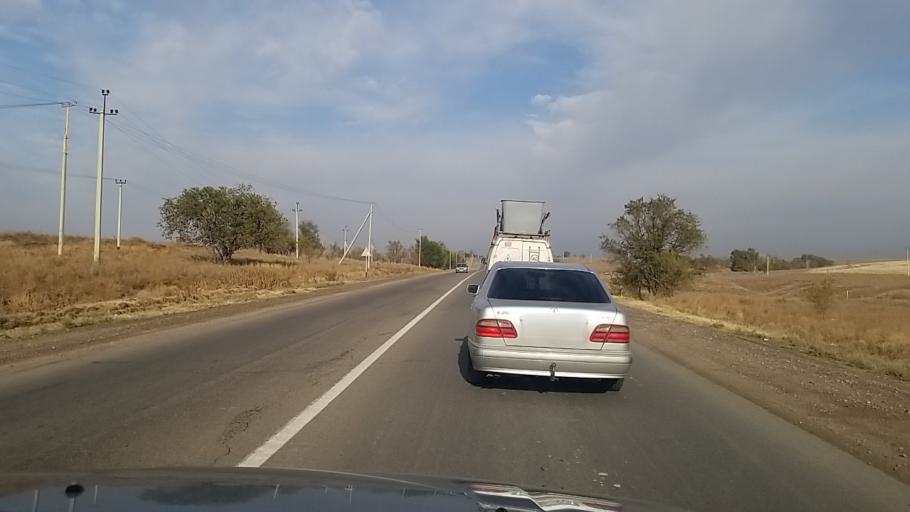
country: KZ
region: Almaty Oblysy
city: Burunday
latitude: 43.4686
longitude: 76.7014
